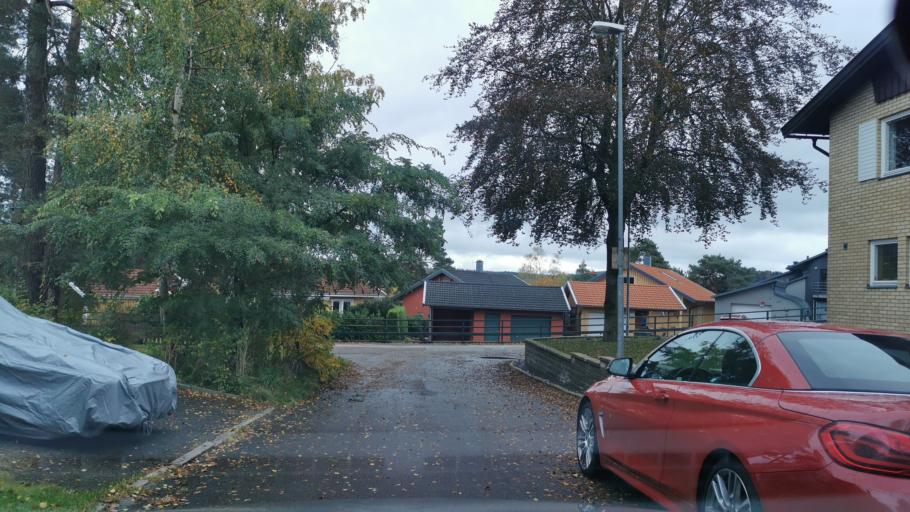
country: SE
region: Vaestra Goetaland
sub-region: Partille Kommun
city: Partille
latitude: 57.7242
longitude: 12.0709
